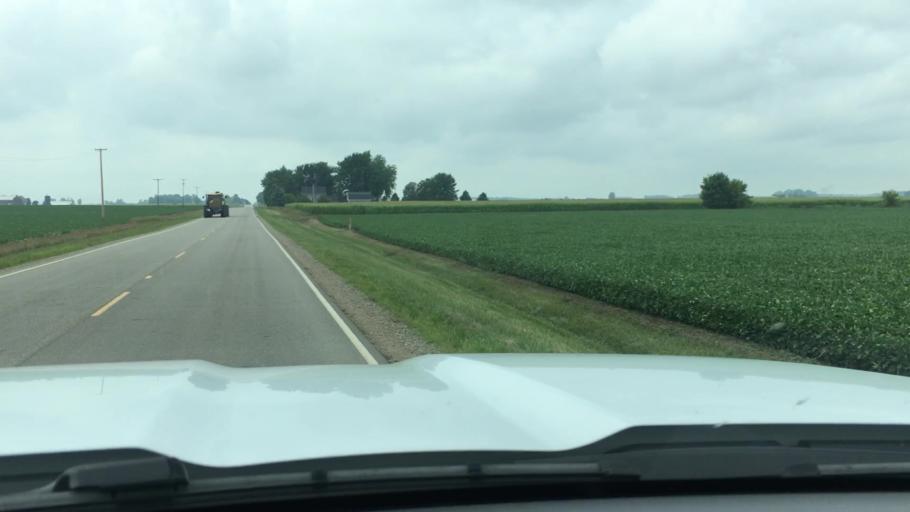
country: US
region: Michigan
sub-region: Sanilac County
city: Marlette
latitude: 43.3589
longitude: -82.9908
